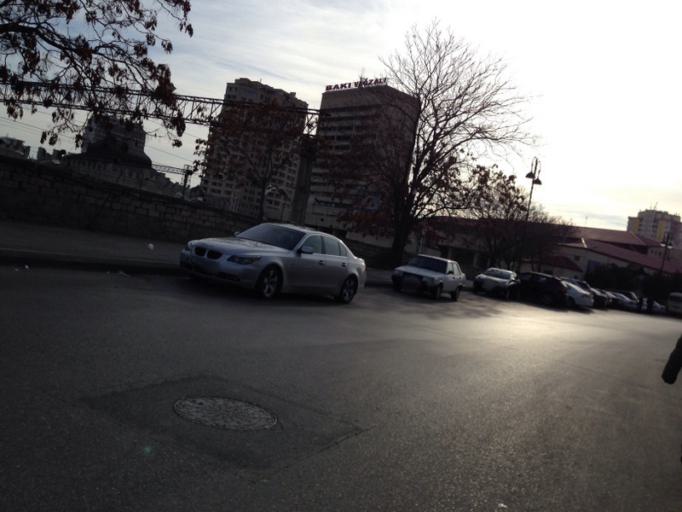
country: AZ
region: Baki
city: Baku
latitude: 40.3815
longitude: 49.8503
